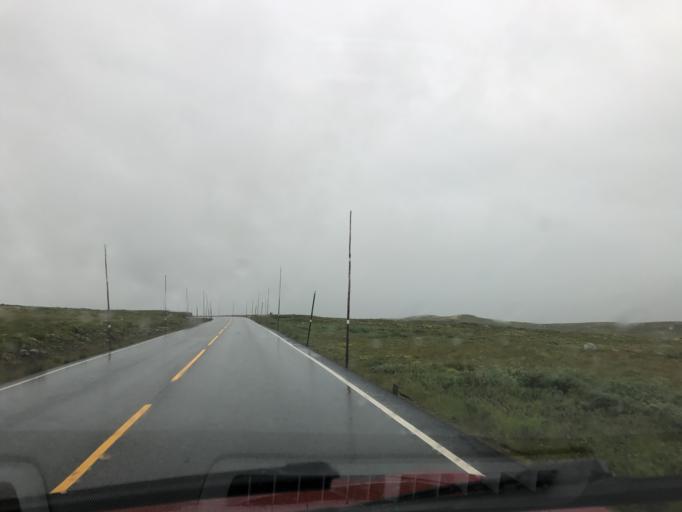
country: NO
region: Hordaland
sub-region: Eidfjord
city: Eidfjord
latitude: 60.3721
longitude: 7.4809
